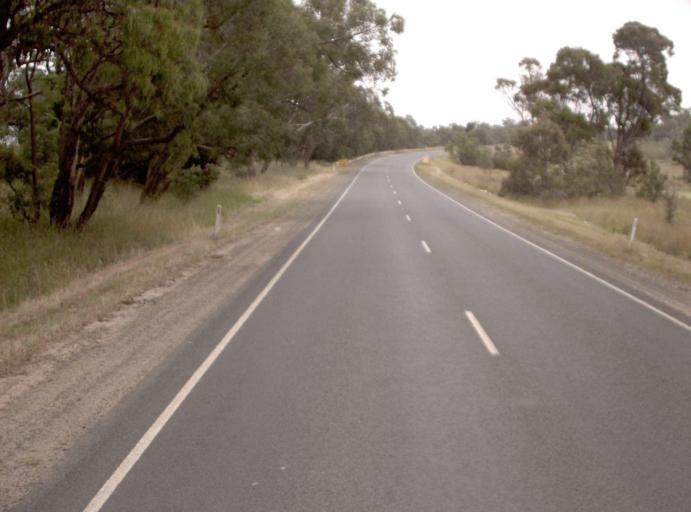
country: AU
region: Victoria
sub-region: Latrobe
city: Traralgon
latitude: -38.2492
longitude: 146.5307
